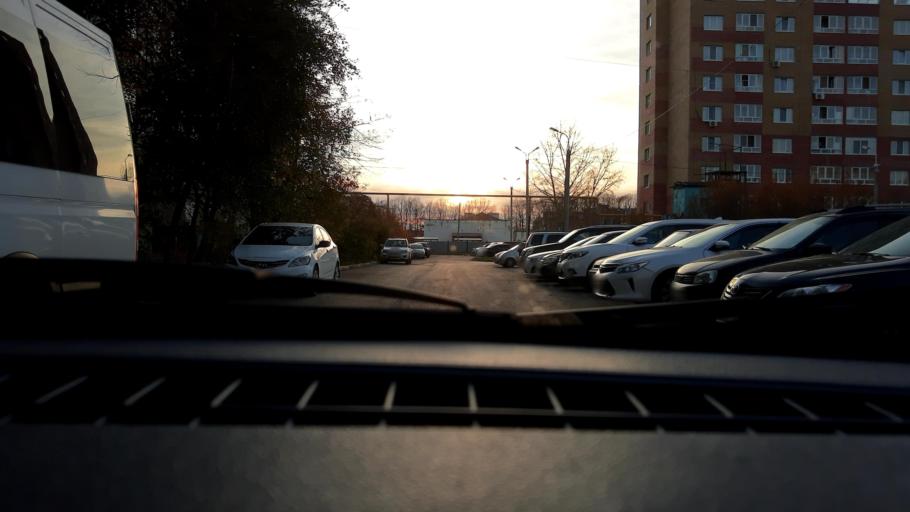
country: RU
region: Bashkortostan
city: Mikhaylovka
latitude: 54.7919
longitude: 55.8632
